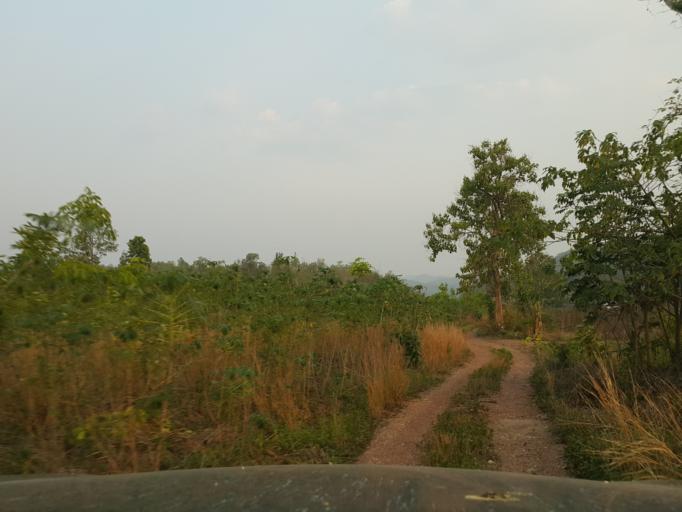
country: TH
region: Lamphun
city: Thung Hua Chang
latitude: 17.9149
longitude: 99.0736
